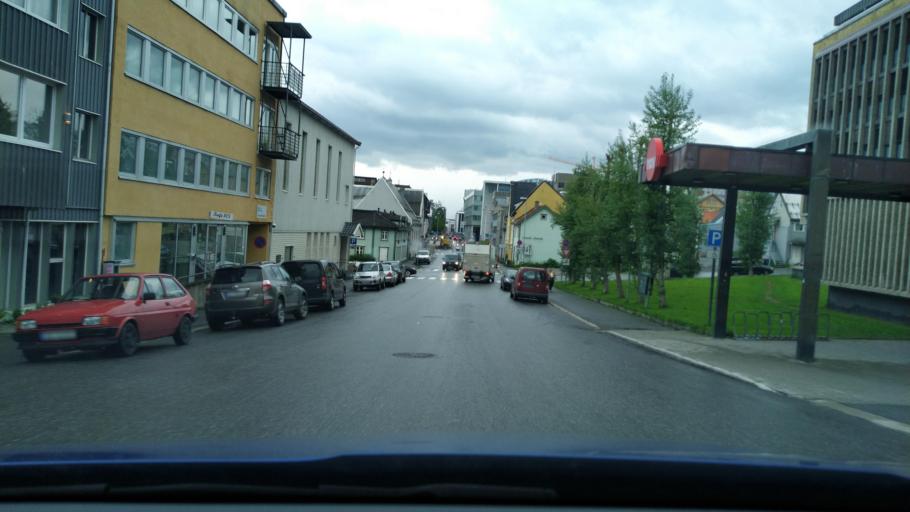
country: NO
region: Troms
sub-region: Tromso
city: Tromso
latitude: 69.6535
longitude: 18.9582
